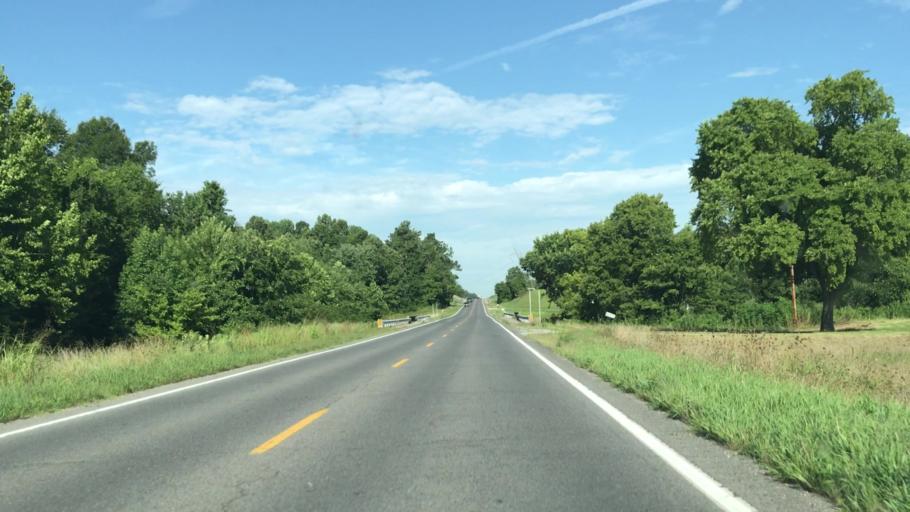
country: US
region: Kentucky
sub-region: Marshall County
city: Calvert City
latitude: 37.0054
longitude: -88.4096
